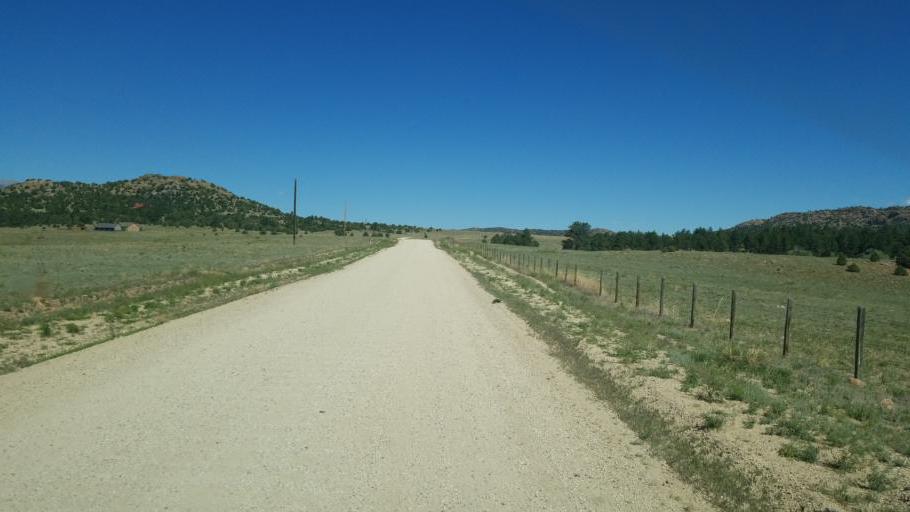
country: US
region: Colorado
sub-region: Custer County
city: Westcliffe
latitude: 38.2173
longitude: -105.4505
